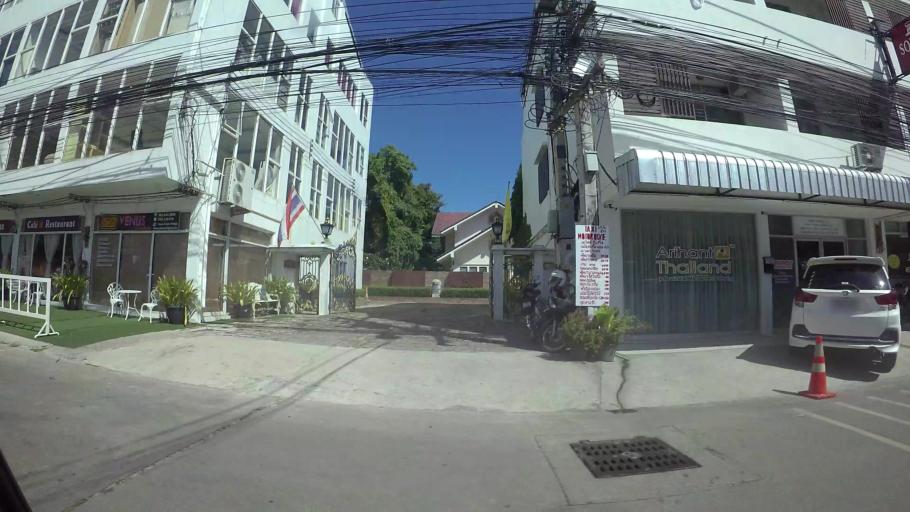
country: TH
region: Chon Buri
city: Phatthaya
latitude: 12.9463
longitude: 100.9023
